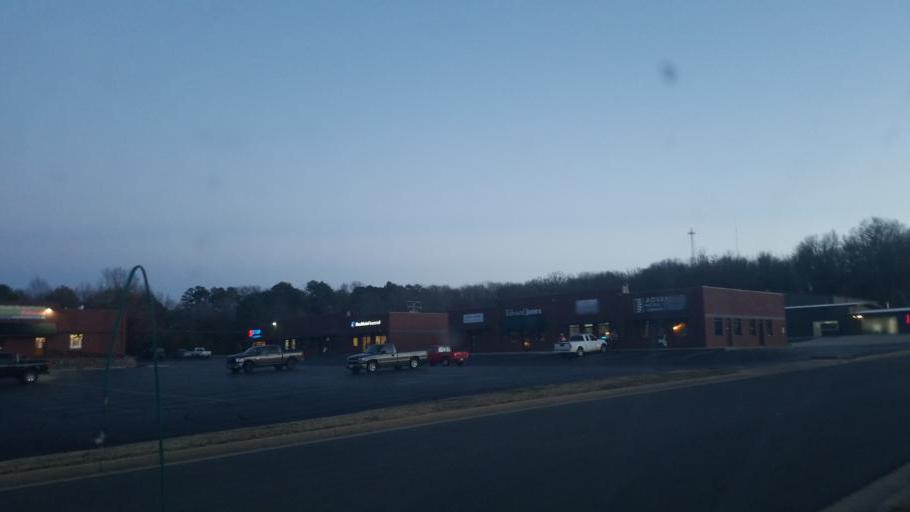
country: US
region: Missouri
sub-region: Howell County
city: West Plains
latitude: 36.7309
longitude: -91.8763
